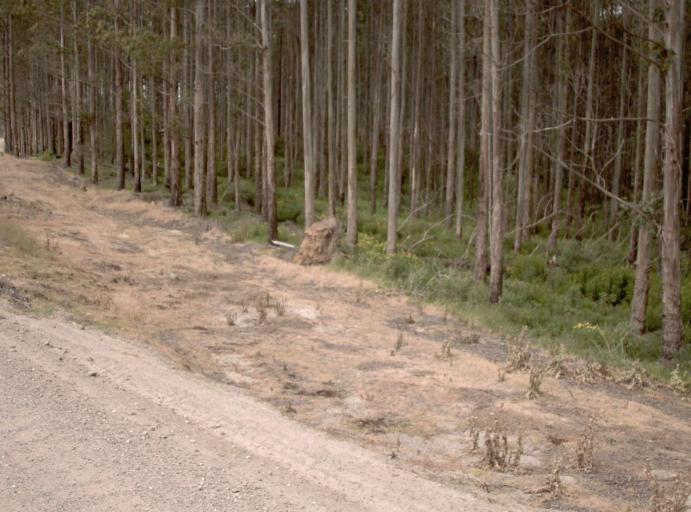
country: AU
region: Victoria
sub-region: Latrobe
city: Traralgon
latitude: -38.3747
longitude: 146.6798
